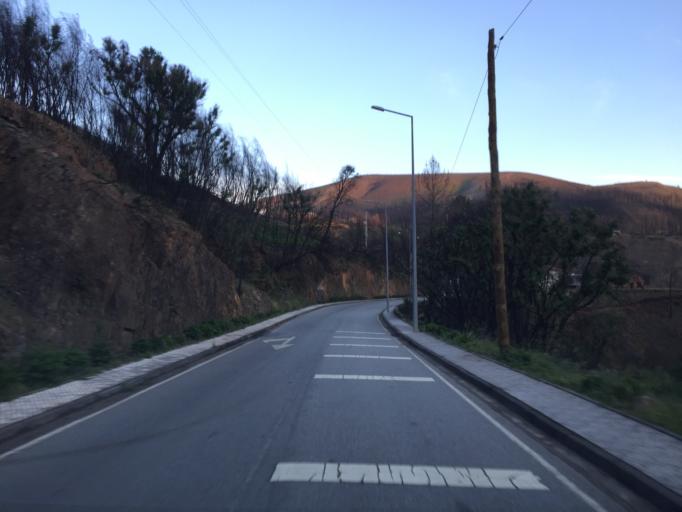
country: PT
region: Coimbra
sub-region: Pampilhosa da Serra
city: Pampilhosa da Serra
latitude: 40.0491
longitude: -7.9604
